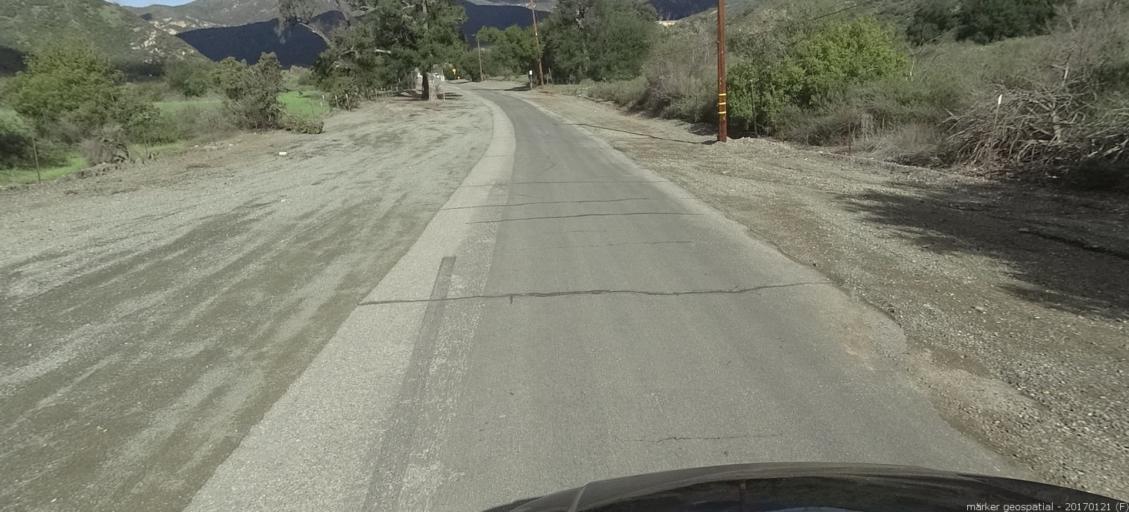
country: US
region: California
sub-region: Orange County
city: Foothill Ranch
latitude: 33.7593
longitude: -117.6768
